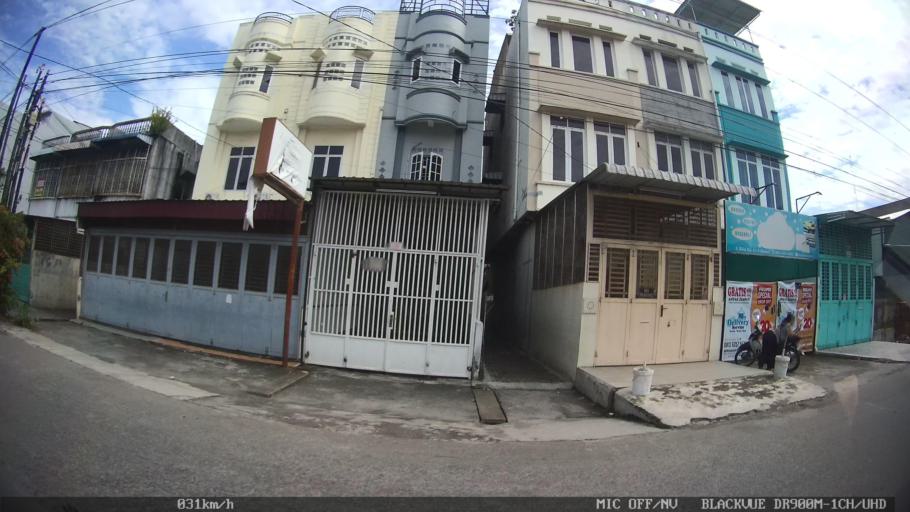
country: ID
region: North Sumatra
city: Medan
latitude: 3.6229
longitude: 98.6801
